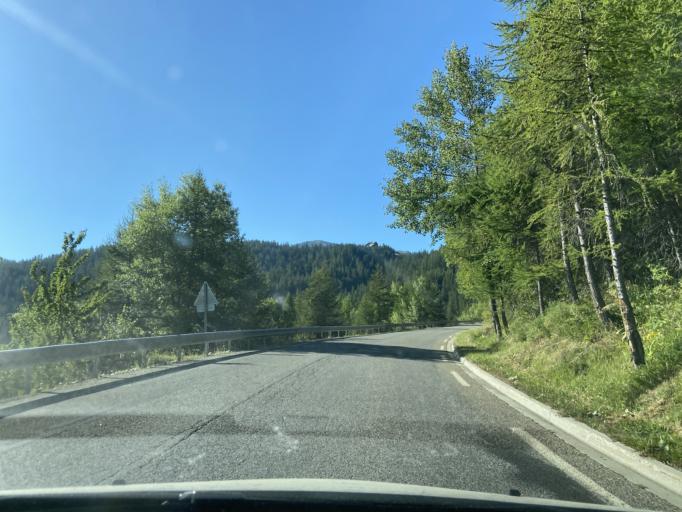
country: FR
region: Provence-Alpes-Cote d'Azur
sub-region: Departement des Hautes-Alpes
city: Guillestre
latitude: 44.6323
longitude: 6.6297
